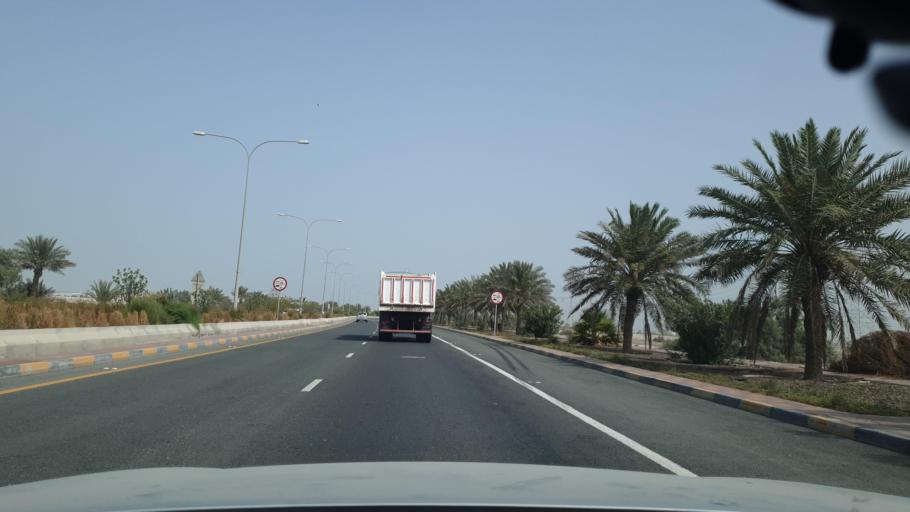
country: QA
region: Al Wakrah
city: Umm Sa'id
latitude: 25.0115
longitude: 51.5555
